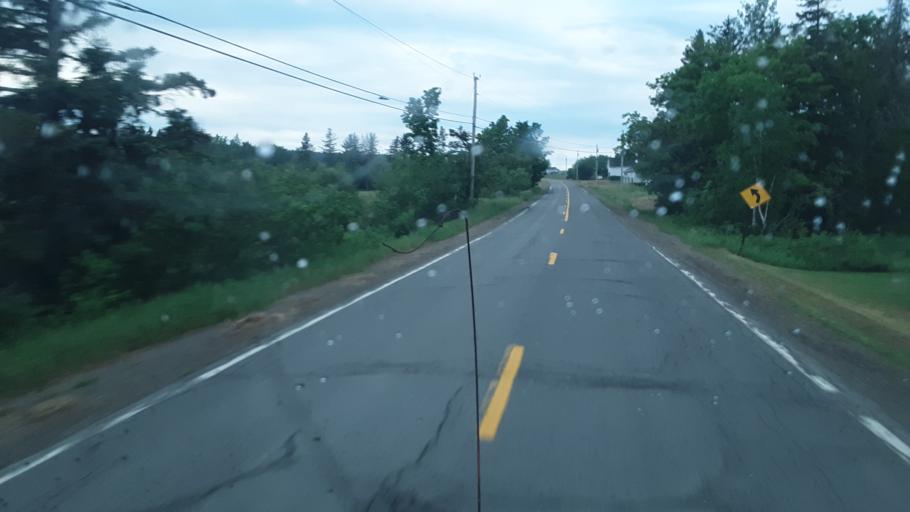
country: US
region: Maine
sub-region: Aroostook County
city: Presque Isle
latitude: 46.7342
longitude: -68.1829
